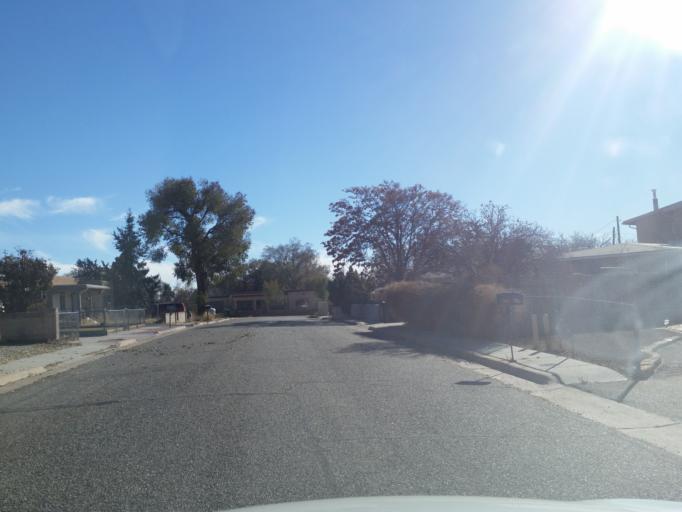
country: US
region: New Mexico
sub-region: Santa Fe County
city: Santa Fe
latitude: 35.6696
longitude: -105.9640
